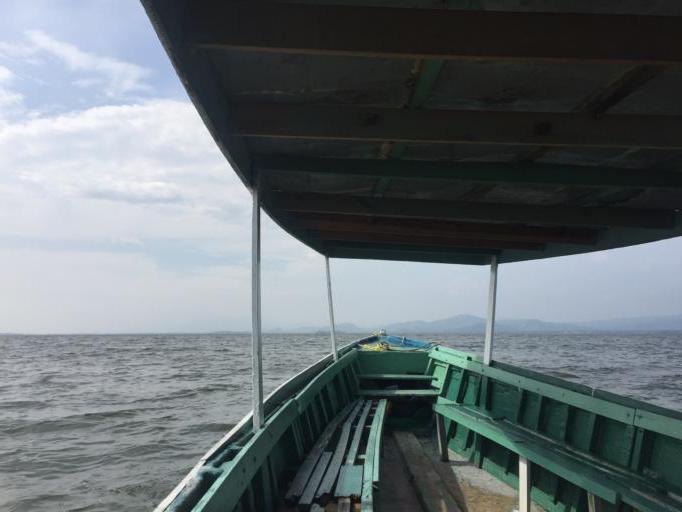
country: MX
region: Guerrero
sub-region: Coyuca de Benitez
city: Colonia Luces en el Mar
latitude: 16.9178
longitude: -99.9827
